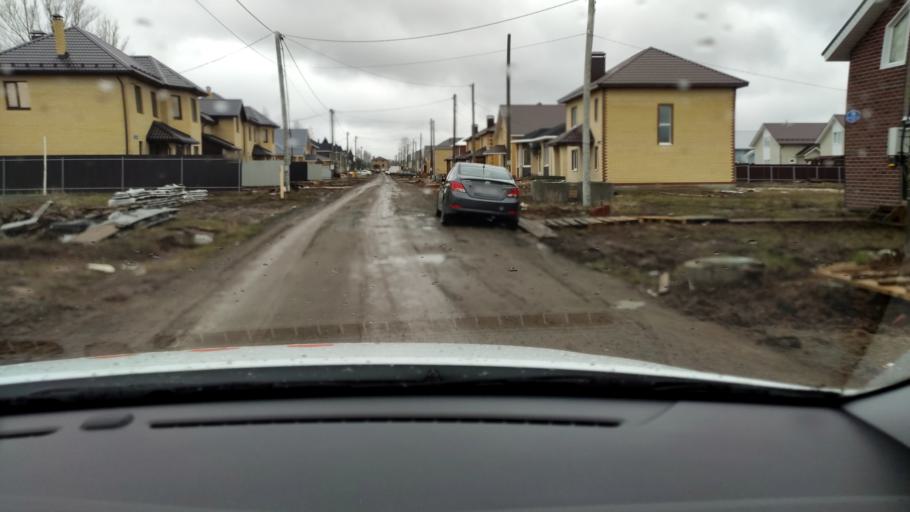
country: RU
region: Tatarstan
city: Stolbishchi
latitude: 55.7189
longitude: 49.3038
